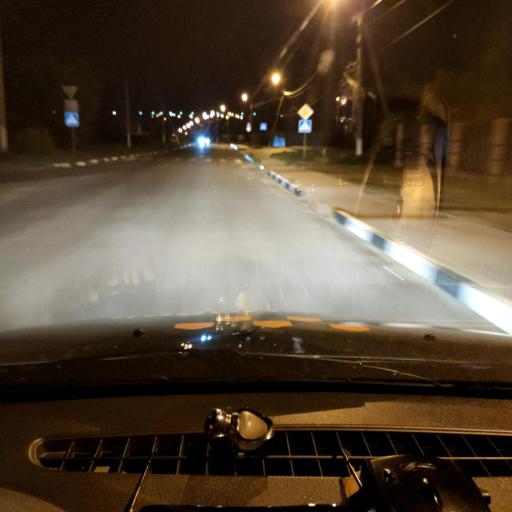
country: RU
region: Belgorod
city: Mayskiy
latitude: 50.5190
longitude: 36.4567
